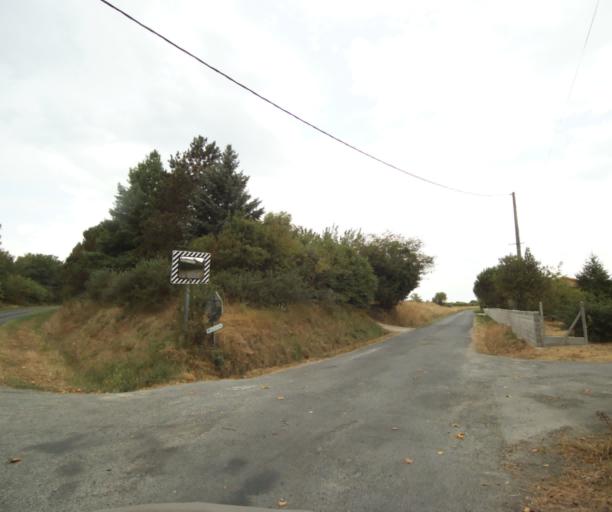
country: FR
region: Aquitaine
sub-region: Departement de la Gironde
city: La Sauve
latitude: 44.7499
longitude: -0.3341
